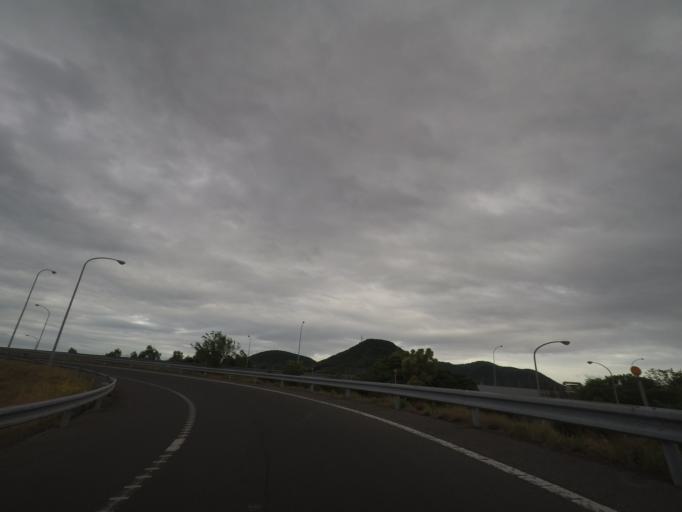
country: JP
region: Kagawa
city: Sakaidecho
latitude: 34.2961
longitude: 133.8439
